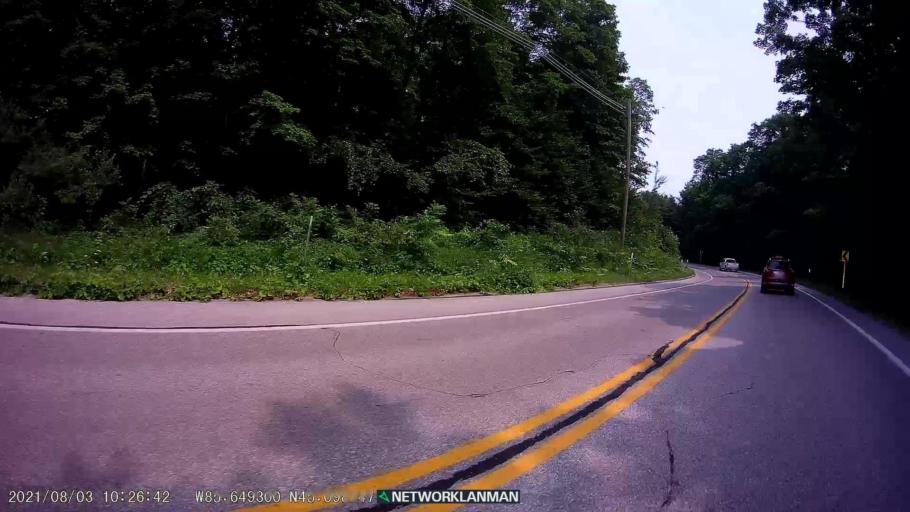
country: US
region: Michigan
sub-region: Leelanau County
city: Leland
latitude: 45.0988
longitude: -85.6490
